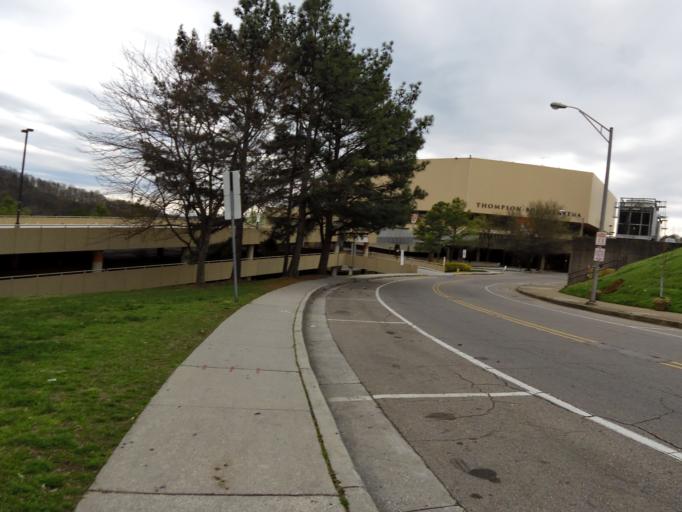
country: US
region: Tennessee
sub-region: Knox County
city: Knoxville
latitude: 35.9532
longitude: -83.9248
